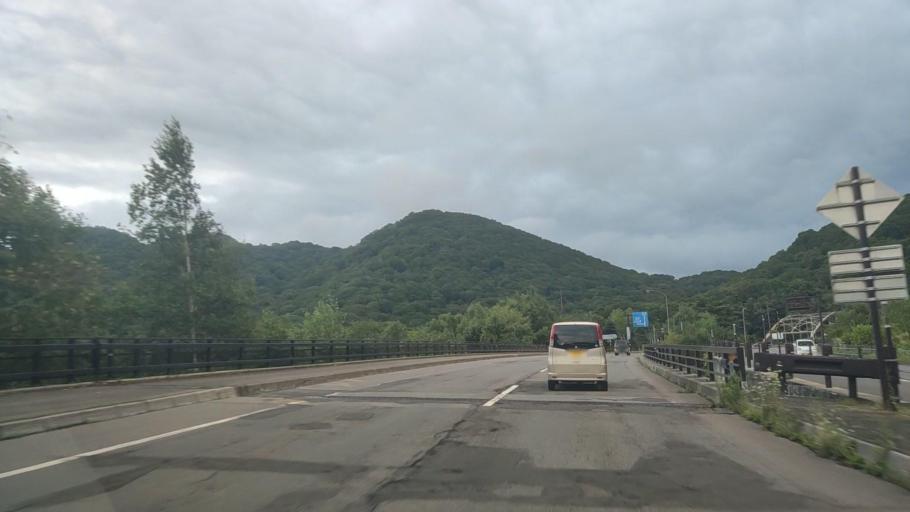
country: JP
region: Hokkaido
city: Nanae
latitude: 41.9582
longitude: 140.6497
